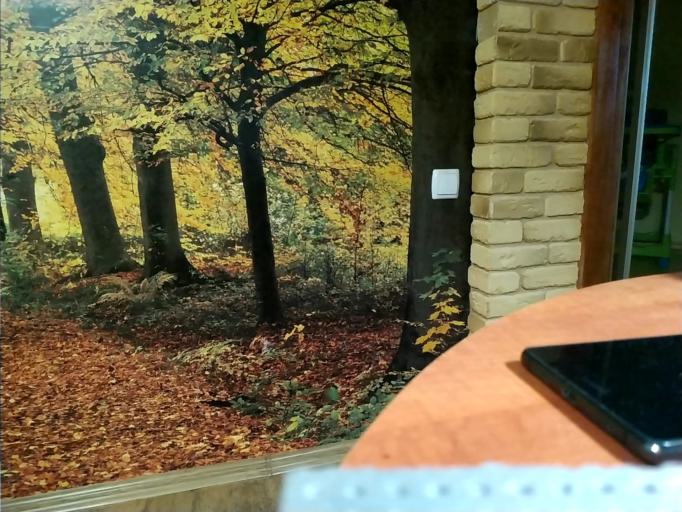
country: RU
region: Moskovskaya
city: Shevlyakovo
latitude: 56.3862
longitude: 36.8604
